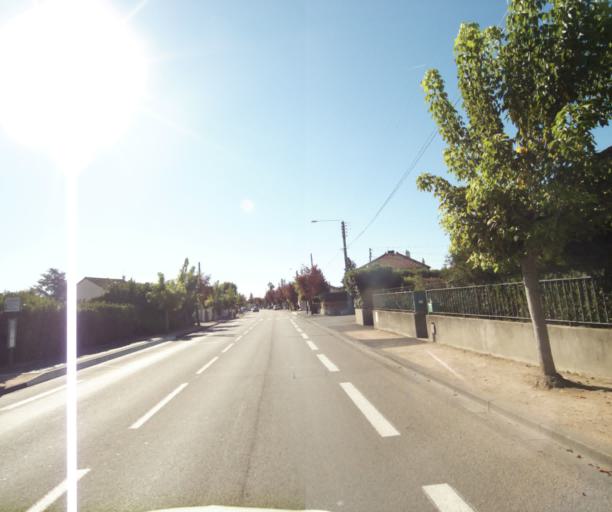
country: FR
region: Auvergne
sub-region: Departement du Puy-de-Dome
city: Cebazat
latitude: 45.8217
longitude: 3.1069
